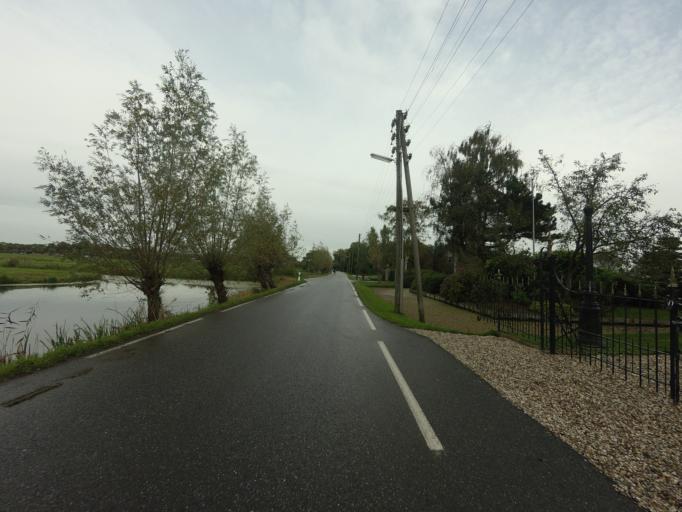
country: NL
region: South Holland
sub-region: Molenwaard
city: Liesveld
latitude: 51.9365
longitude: 4.7732
